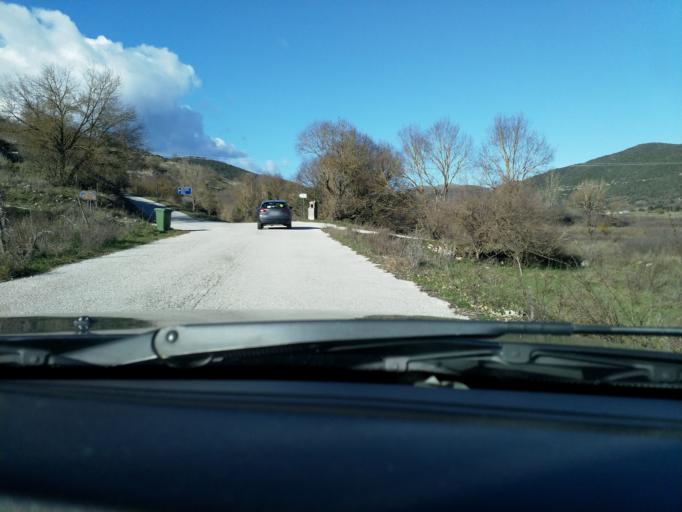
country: GR
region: Epirus
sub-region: Nomos Ioanninon
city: Kalpaki
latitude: 39.8798
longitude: 20.6784
